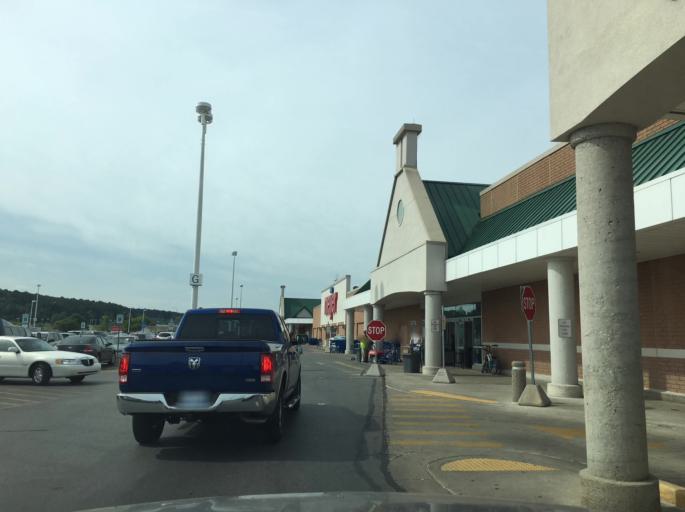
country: US
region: Michigan
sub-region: Grand Traverse County
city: Traverse City
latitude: 44.7438
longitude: -85.6439
